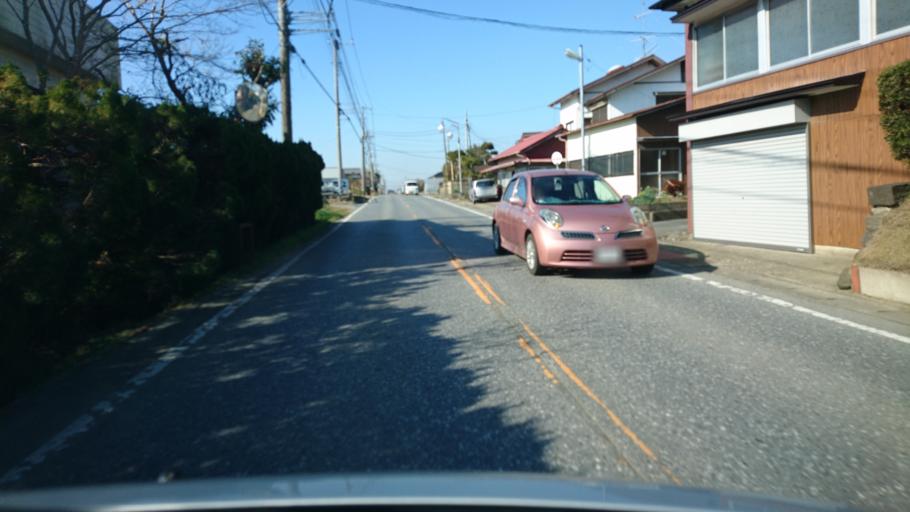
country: JP
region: Chiba
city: Kimitsu
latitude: 35.3020
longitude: 139.9732
